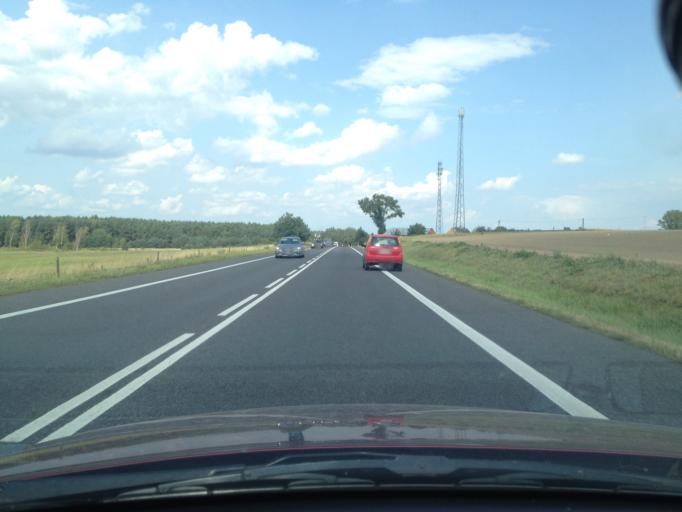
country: PL
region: West Pomeranian Voivodeship
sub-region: Powiat goleniowski
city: Przybiernow
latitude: 53.7619
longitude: 14.7787
